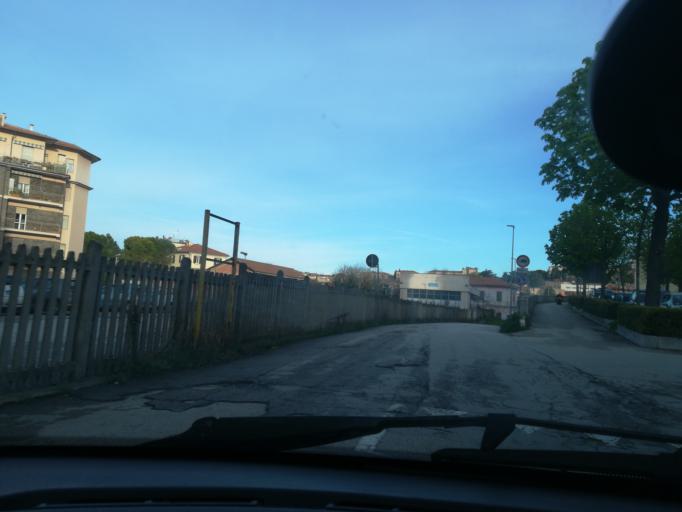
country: IT
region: The Marches
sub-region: Provincia di Macerata
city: Macerata
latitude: 43.2937
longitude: 13.4550
